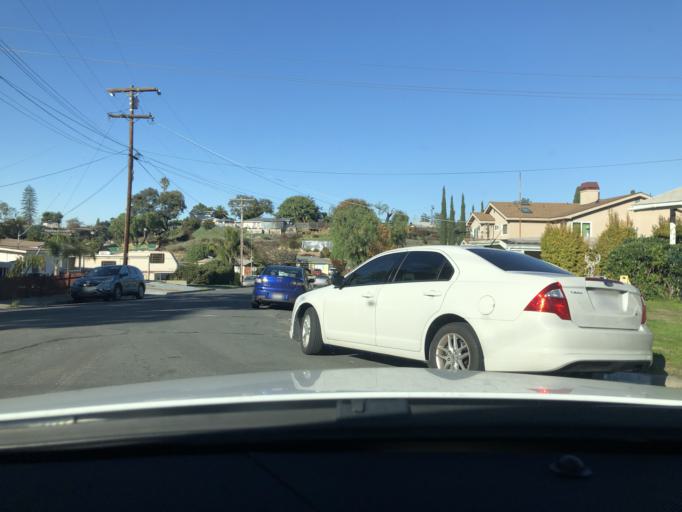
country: US
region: California
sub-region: San Diego County
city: Lemon Grove
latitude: 32.7431
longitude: -117.0621
